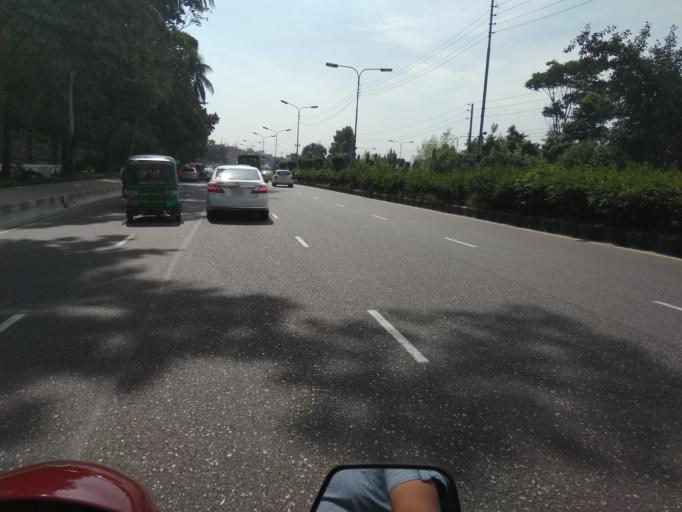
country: BD
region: Dhaka
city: Azimpur
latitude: 23.7677
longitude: 90.3892
